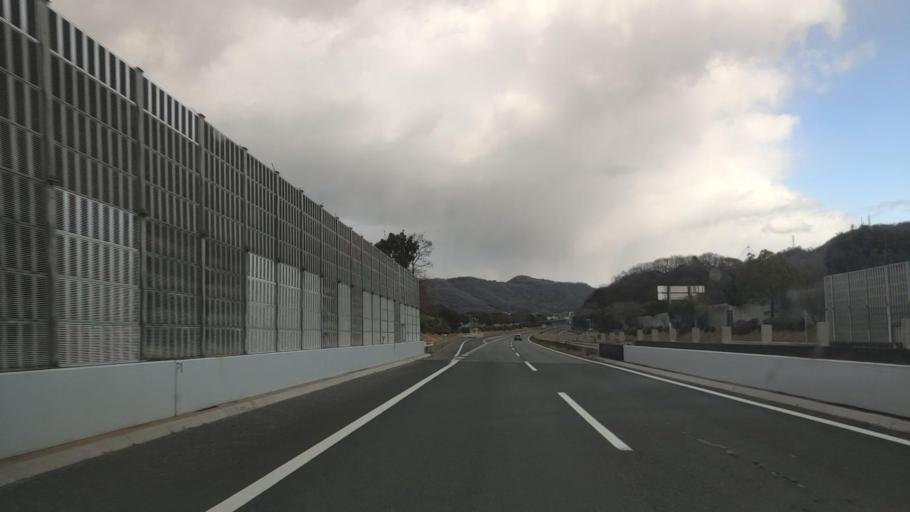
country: JP
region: Hiroshima
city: Fukuyama
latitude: 34.5154
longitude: 133.3649
